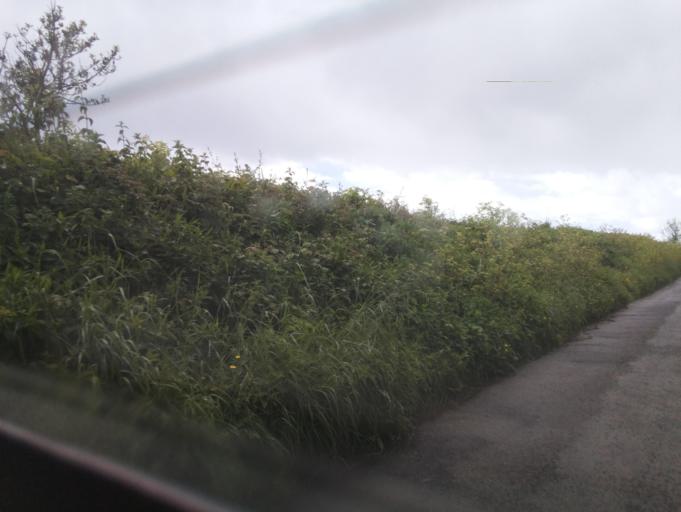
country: GB
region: England
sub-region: Devon
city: Dartmouth
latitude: 50.3541
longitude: -3.5537
